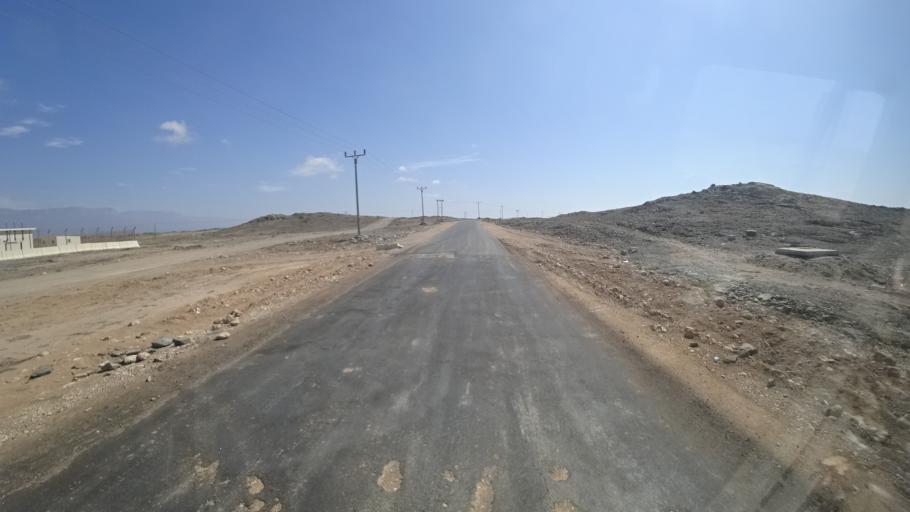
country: OM
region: Zufar
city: Salalah
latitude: 16.9660
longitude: 54.7506
